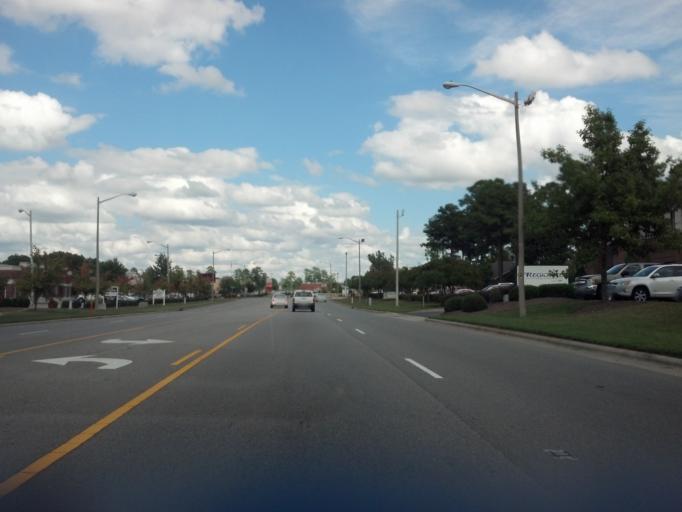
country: US
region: North Carolina
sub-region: Pitt County
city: Windsor
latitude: 35.5624
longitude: -77.3626
